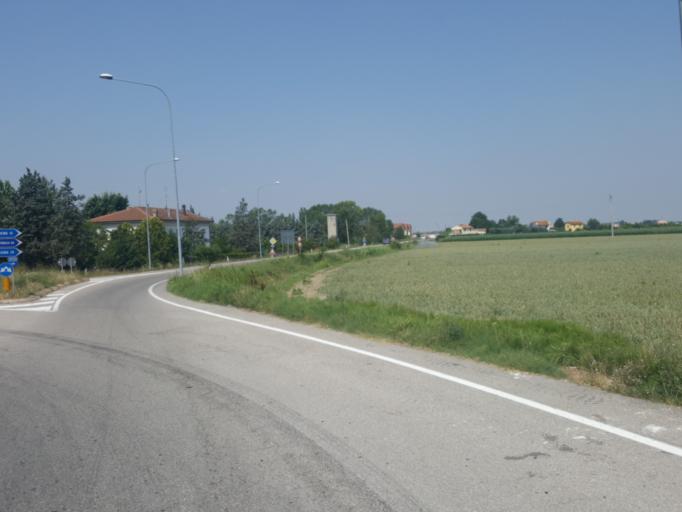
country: IT
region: Emilia-Romagna
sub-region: Provincia di Ravenna
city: Massa Lombarda
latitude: 44.4569
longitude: 11.7946
